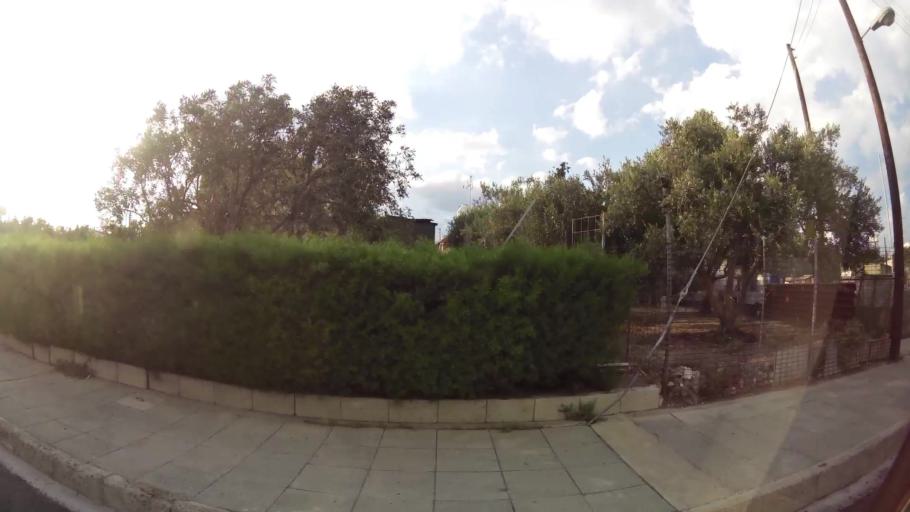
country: CY
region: Larnaka
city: Dhromolaxia
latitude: 34.8705
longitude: 33.5869
